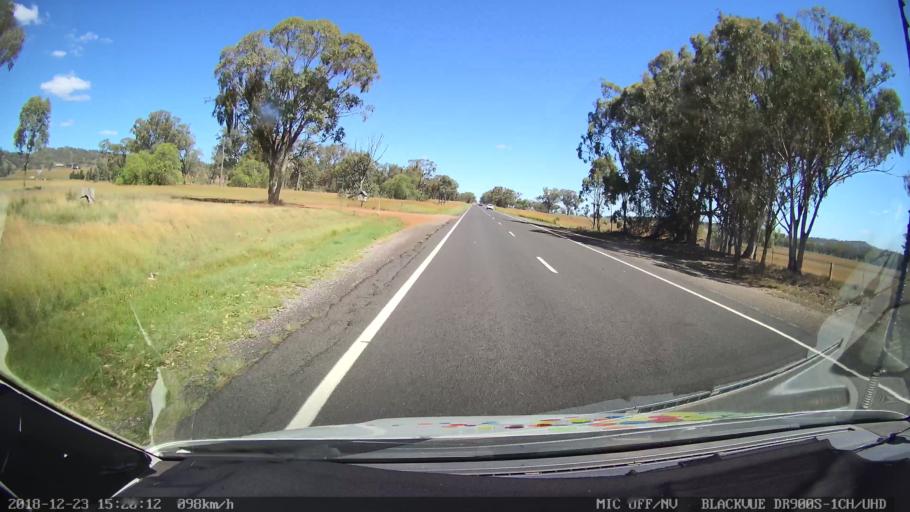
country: AU
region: New South Wales
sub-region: Tamworth Municipality
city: Manilla
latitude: -30.8394
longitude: 150.7881
